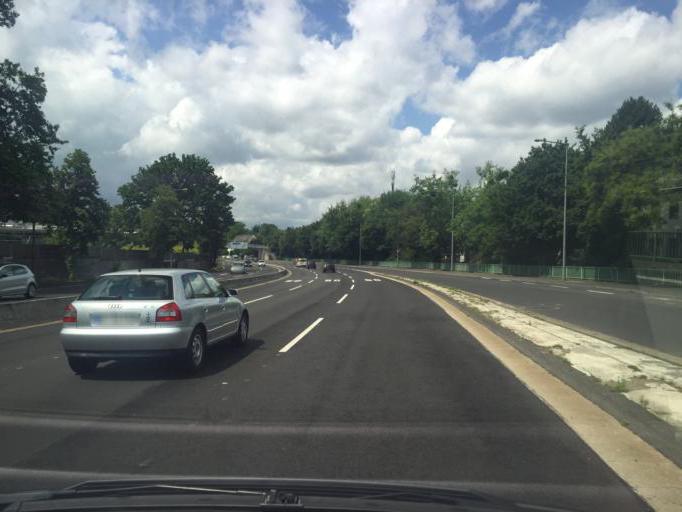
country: DE
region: North Rhine-Westphalia
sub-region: Regierungsbezirk Koln
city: Riehl
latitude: 50.9589
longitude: 6.9671
